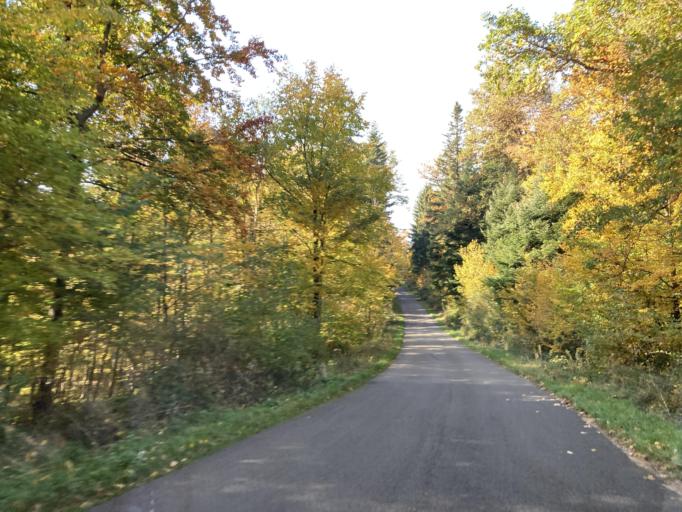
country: DE
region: Baden-Wuerttemberg
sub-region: Tuebingen Region
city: Mossingen
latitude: 48.3832
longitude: 9.0645
